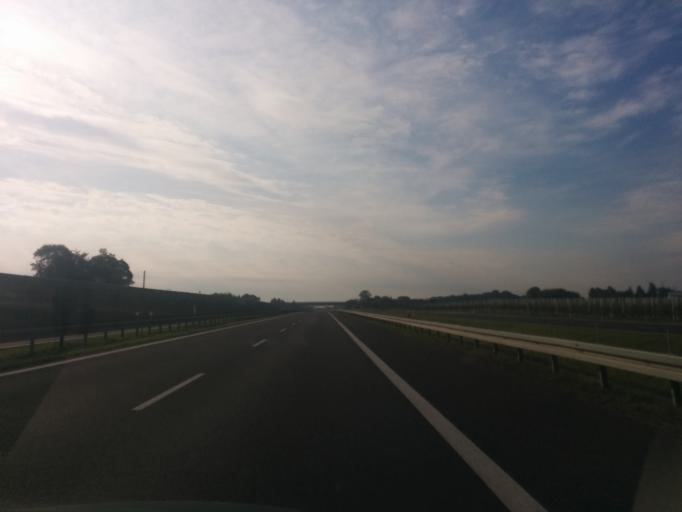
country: PL
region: Masovian Voivodeship
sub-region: Powiat grojecki
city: Jasieniec
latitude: 51.8028
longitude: 20.8882
